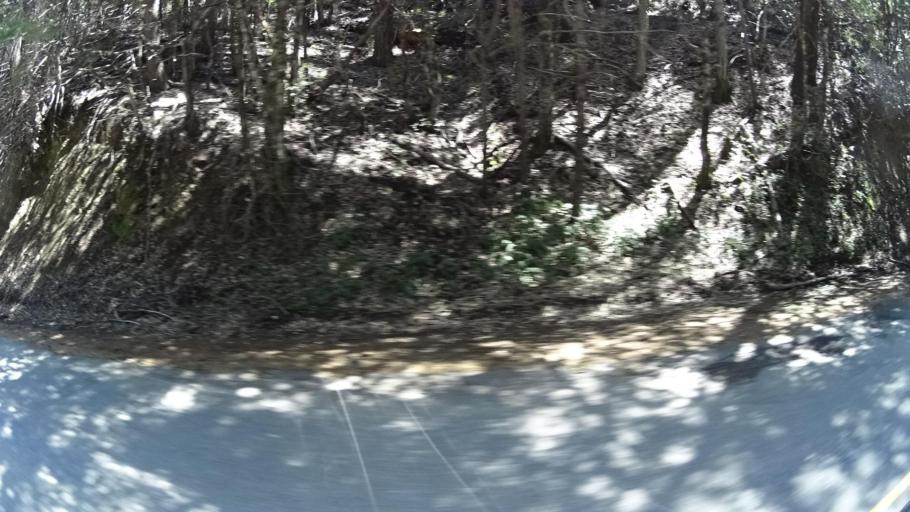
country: US
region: California
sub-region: Humboldt County
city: Rio Dell
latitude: 40.2848
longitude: -124.0608
